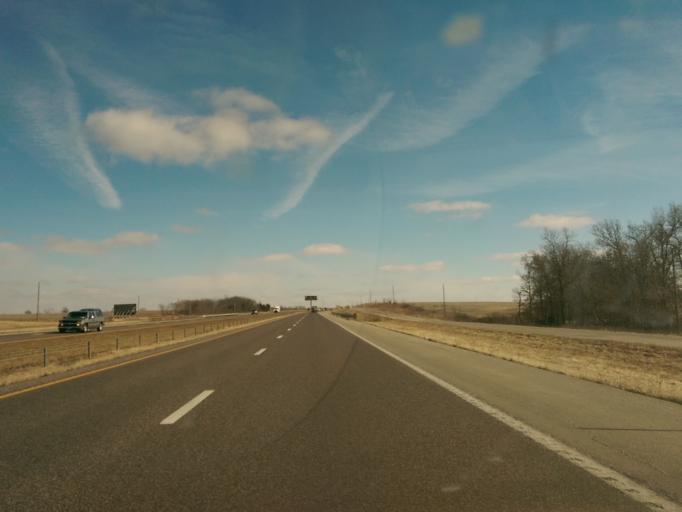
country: US
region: Missouri
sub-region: Callaway County
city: Fulton
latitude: 38.9436
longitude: -91.8868
